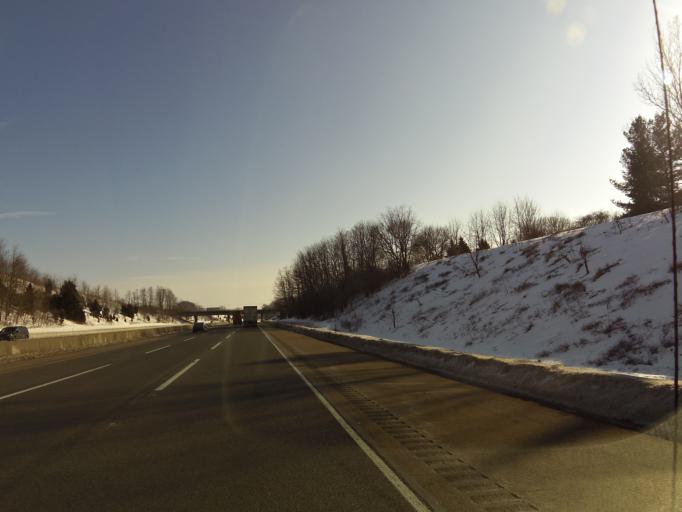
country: US
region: Illinois
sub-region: Winnebago County
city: Roscoe
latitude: 42.4305
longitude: -88.9875
